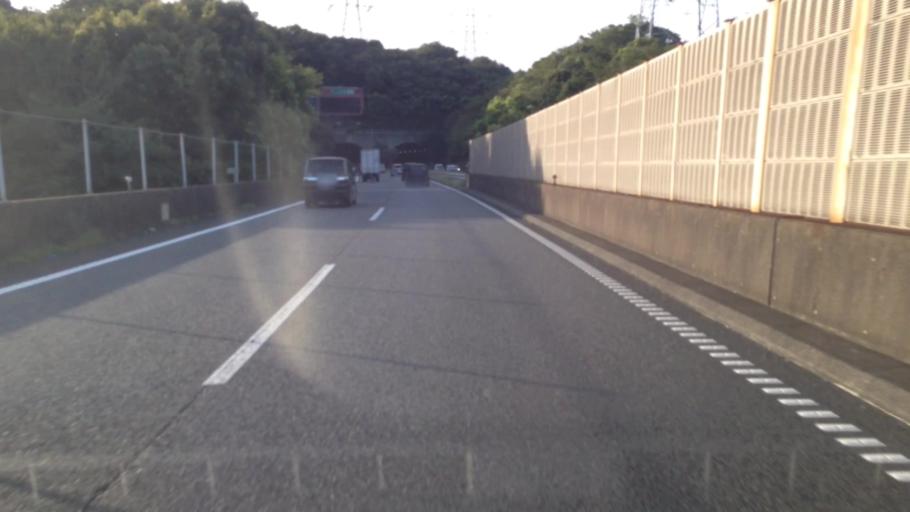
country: JP
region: Kanagawa
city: Zushi
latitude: 35.3209
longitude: 139.6041
